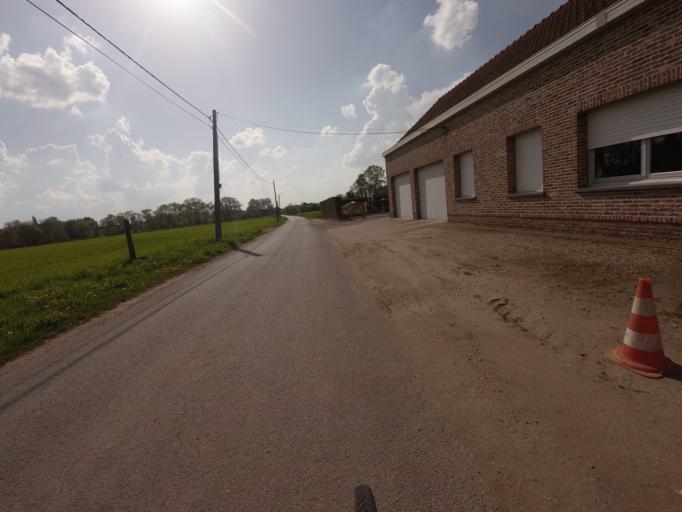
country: BE
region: Flanders
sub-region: Provincie Antwerpen
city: Putte
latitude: 51.0759
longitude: 4.6625
